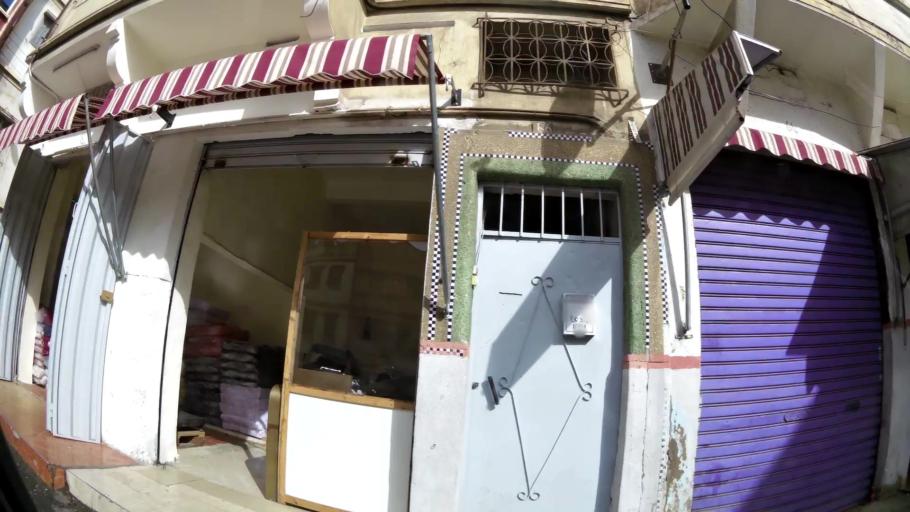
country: MA
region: Grand Casablanca
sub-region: Casablanca
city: Casablanca
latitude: 33.5686
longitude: -7.5857
